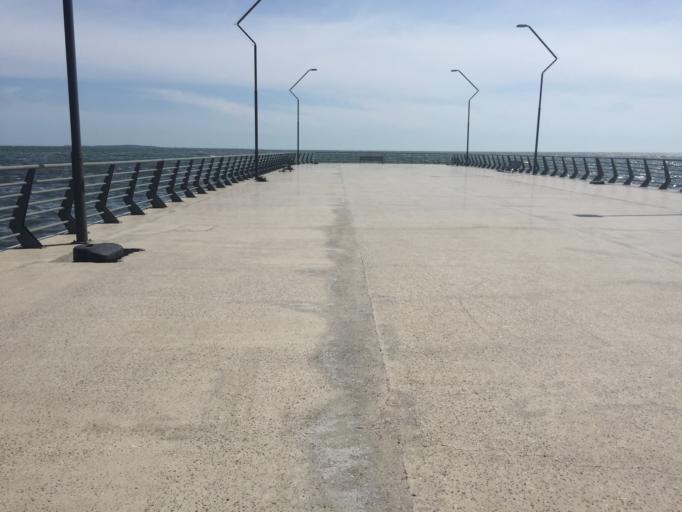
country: AZ
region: Baki
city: Baku
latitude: 40.3736
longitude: 49.8825
